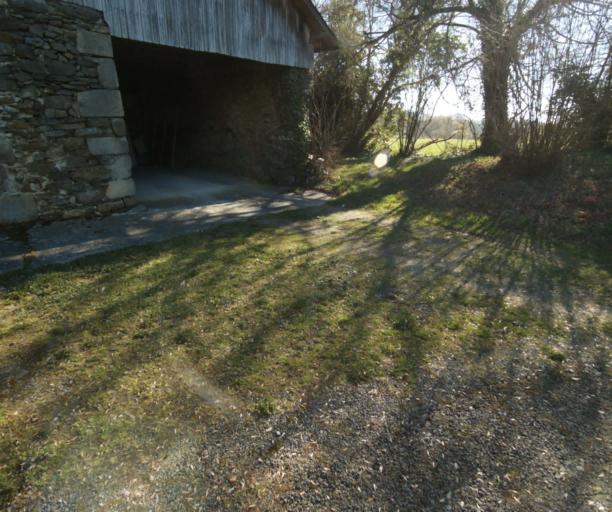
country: FR
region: Limousin
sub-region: Departement de la Correze
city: Seilhac
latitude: 45.3973
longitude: 1.7073
